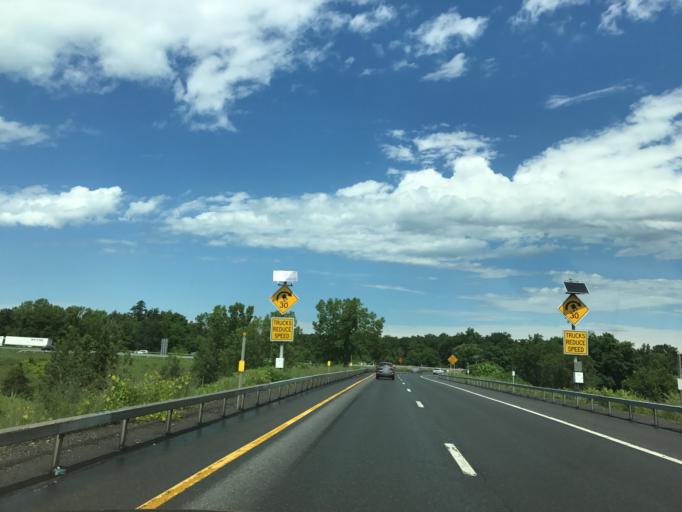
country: US
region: New York
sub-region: Albany County
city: McKownville
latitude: 42.6964
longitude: -73.8358
